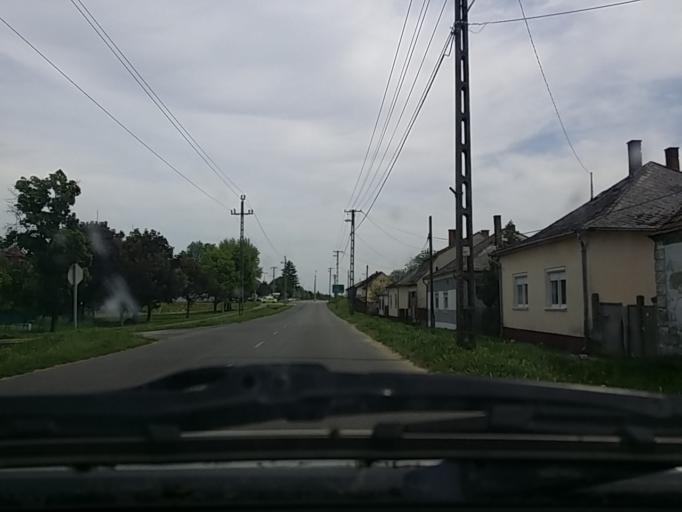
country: HU
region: Somogy
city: Barcs
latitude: 45.9660
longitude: 17.4563
